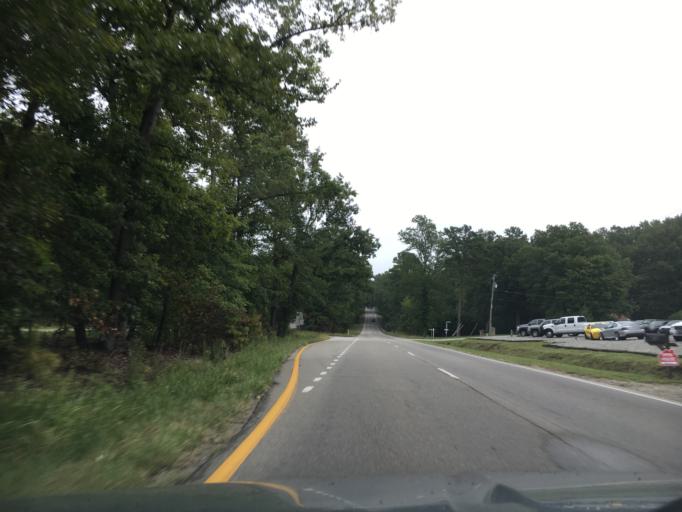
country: US
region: Virginia
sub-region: Chesterfield County
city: Woodlake
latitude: 37.5091
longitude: -77.7567
